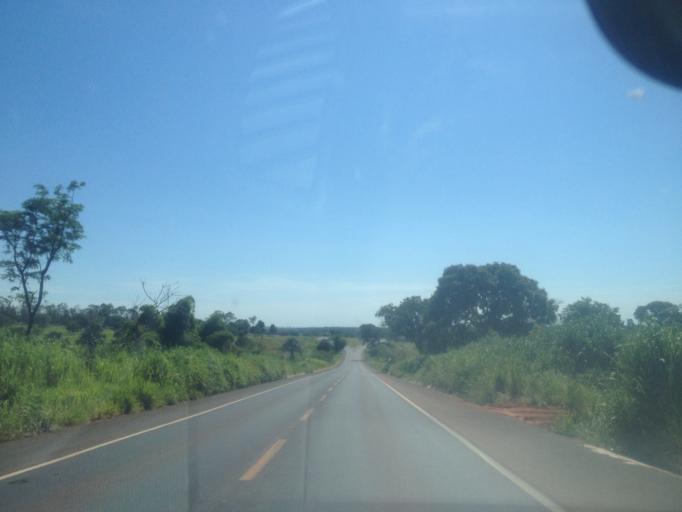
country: BR
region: Minas Gerais
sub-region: Santa Vitoria
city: Santa Vitoria
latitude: -18.8780
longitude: -50.1276
